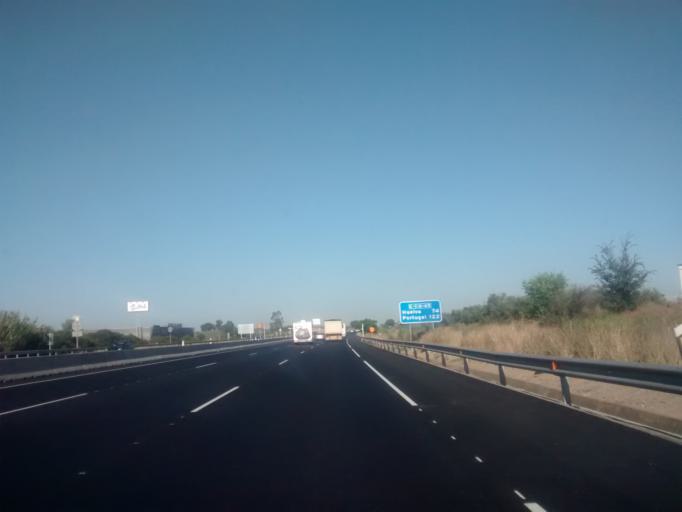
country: ES
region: Andalusia
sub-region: Provincia de Sevilla
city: Umbrete
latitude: 37.3591
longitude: -6.1475
